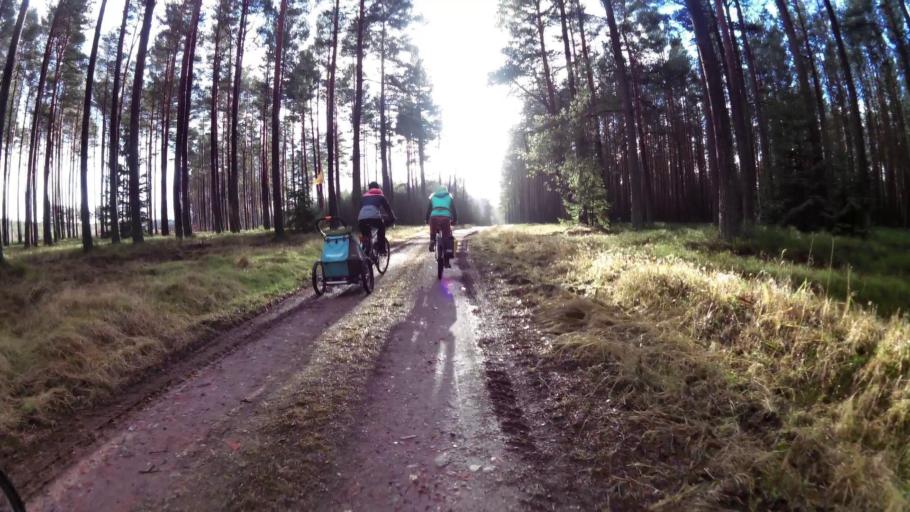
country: PL
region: West Pomeranian Voivodeship
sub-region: Powiat koszalinski
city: Sianow
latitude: 54.0881
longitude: 16.2932
